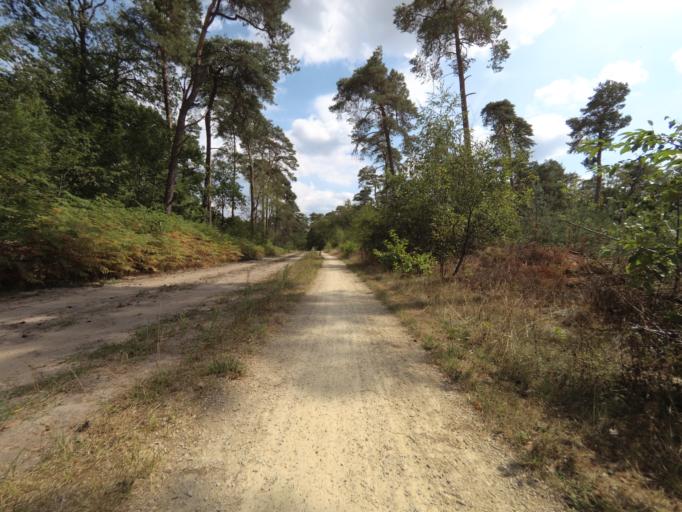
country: NL
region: Overijssel
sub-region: Gemeente Haaksbergen
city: Haaksbergen
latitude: 52.1278
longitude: 6.7143
